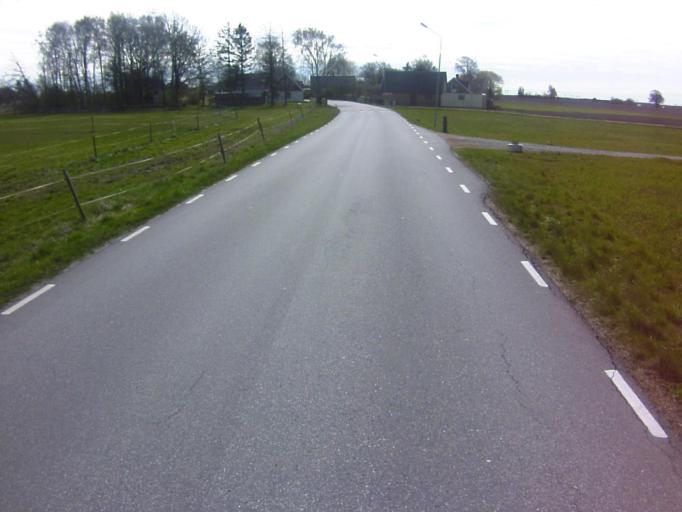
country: SE
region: Skane
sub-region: Kavlinge Kommun
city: Hofterup
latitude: 55.7887
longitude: 12.9712
